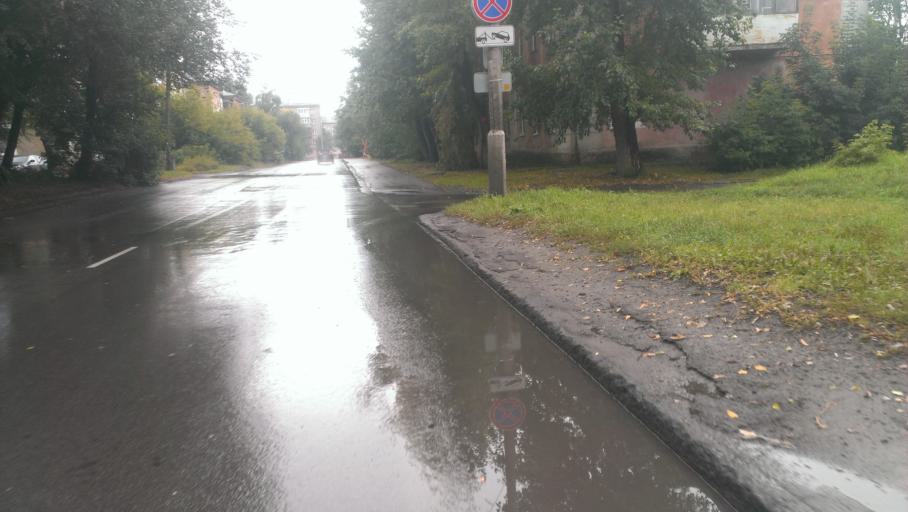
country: RU
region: Altai Krai
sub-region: Gorod Barnaulskiy
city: Barnaul
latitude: 53.3586
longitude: 83.7633
